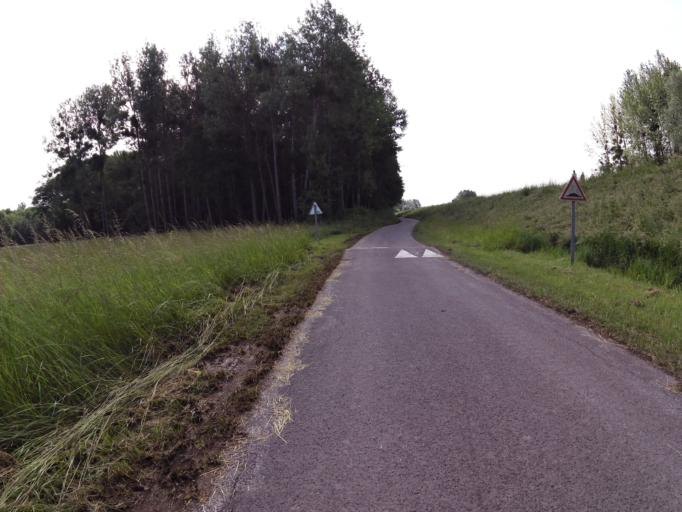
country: FR
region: Champagne-Ardenne
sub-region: Departement de l'Aube
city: Verrieres
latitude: 48.2707
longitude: 4.1671
